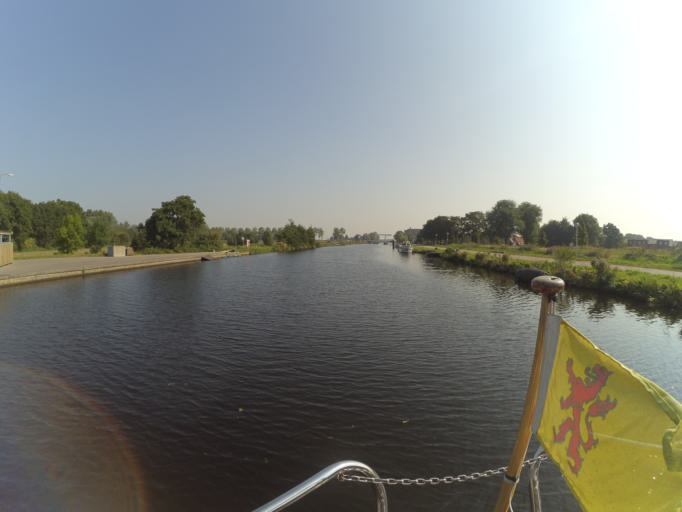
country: NL
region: North Holland
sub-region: Gemeente Heemstede
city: Heemstede
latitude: 52.3374
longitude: 4.6309
